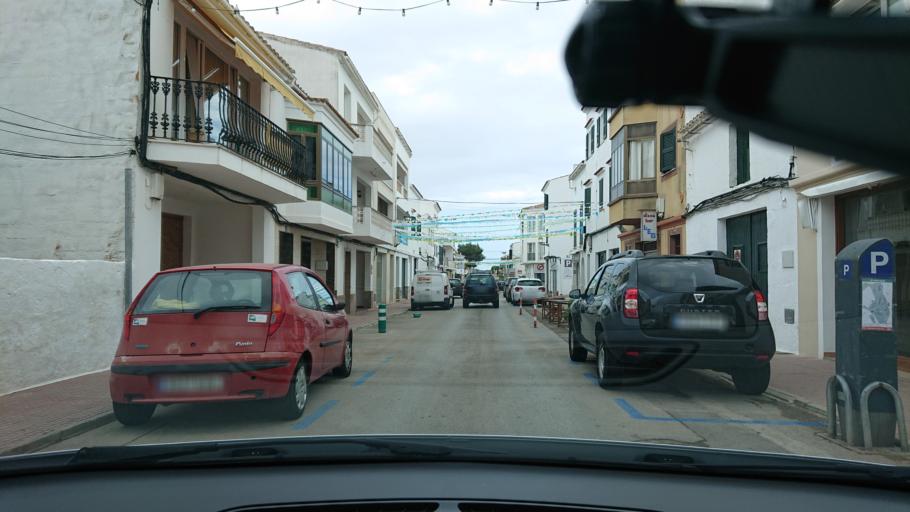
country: ES
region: Balearic Islands
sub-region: Illes Balears
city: Mercadal
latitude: 39.9899
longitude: 4.0937
